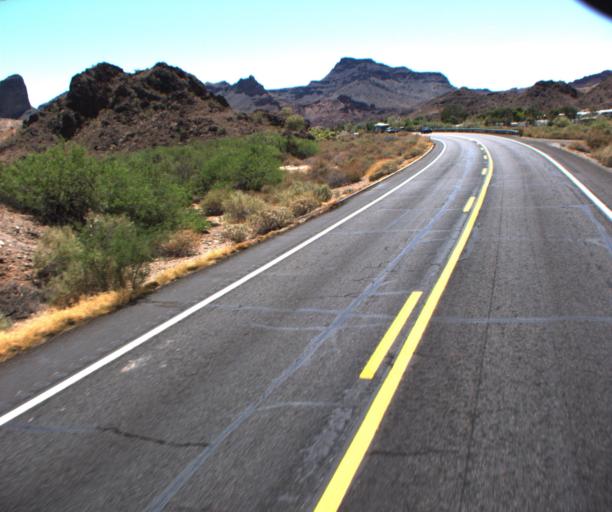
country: US
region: Arizona
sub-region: La Paz County
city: Cienega Springs
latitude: 34.2706
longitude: -114.1329
